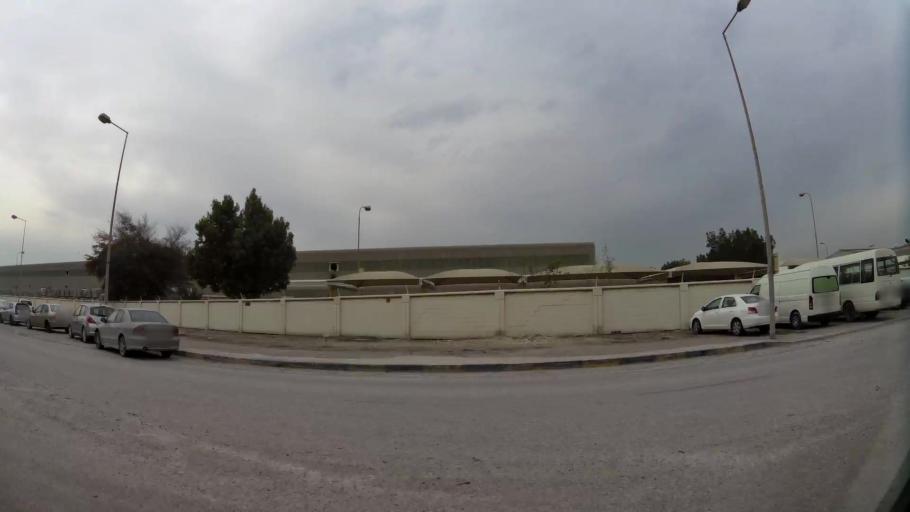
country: BH
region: Northern
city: Sitrah
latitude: 26.1789
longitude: 50.6154
